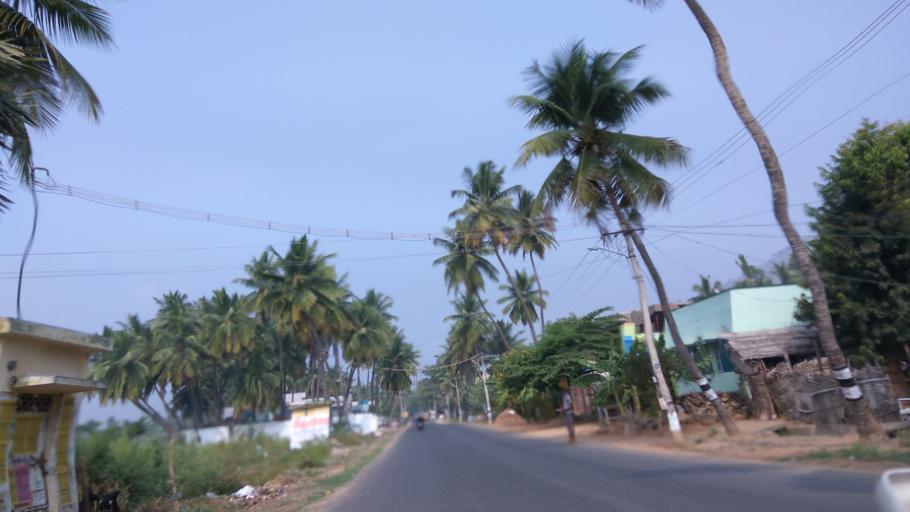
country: IN
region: Tamil Nadu
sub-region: Krishnagiri
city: Krishnagiri
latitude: 12.4696
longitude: 78.2006
